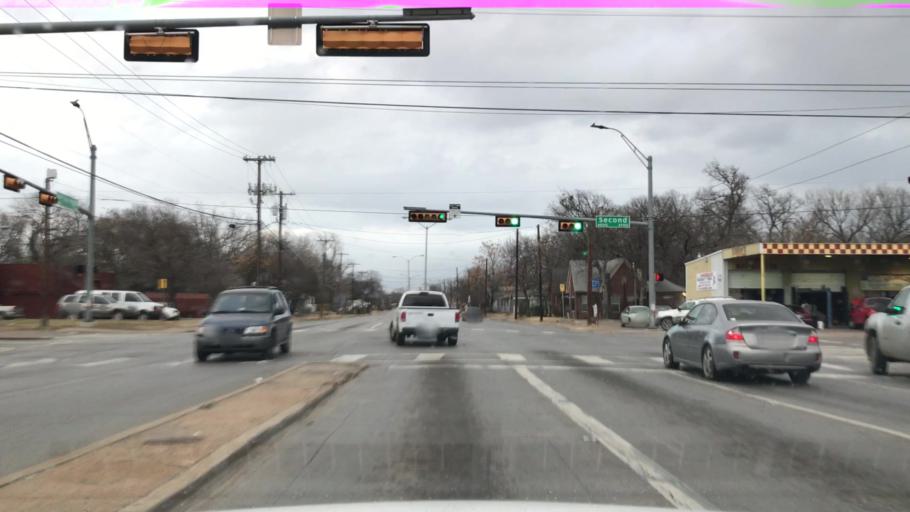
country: US
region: Texas
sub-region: Dallas County
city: Dallas
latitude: 32.7618
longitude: -96.7459
